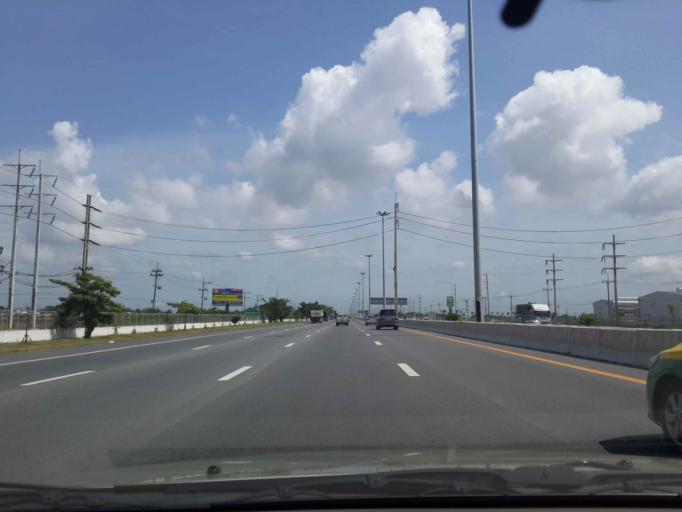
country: TH
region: Chachoengsao
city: Bang Pakong
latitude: 13.5642
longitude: 100.9878
